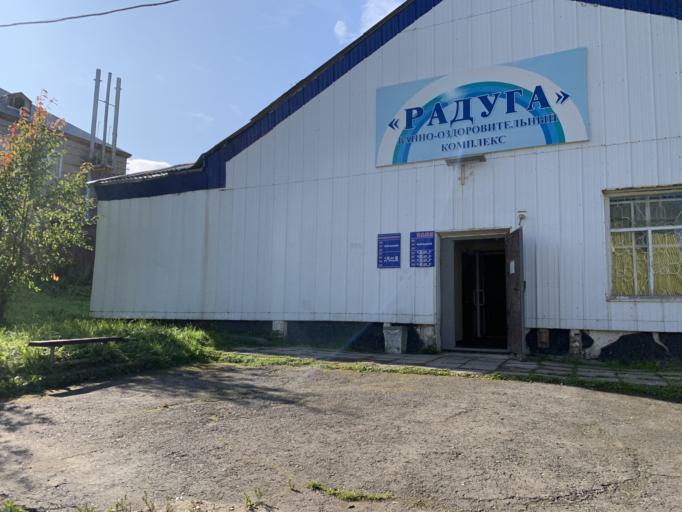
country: RU
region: Perm
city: Gubakha
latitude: 58.8432
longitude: 57.5550
